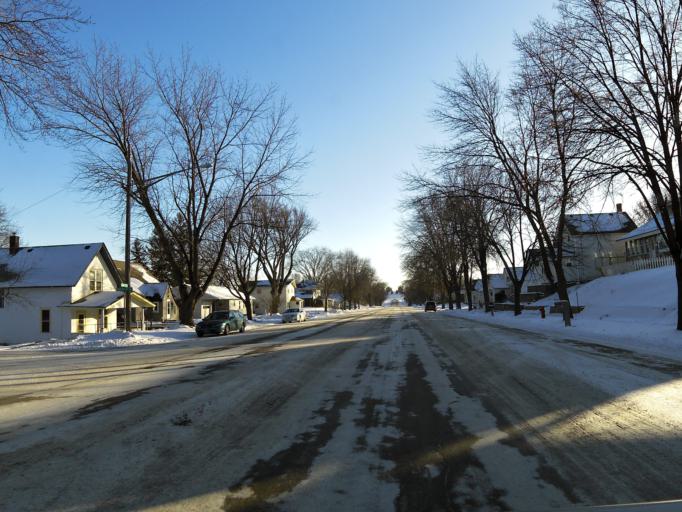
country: US
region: Minnesota
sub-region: Rice County
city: Lonsdale
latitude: 44.4792
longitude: -93.4286
